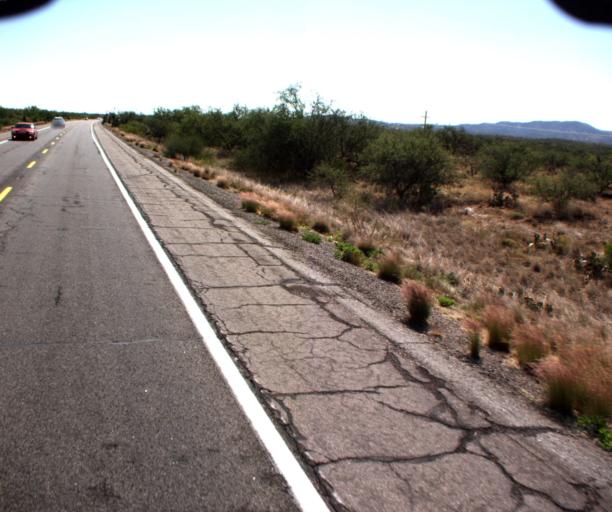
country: US
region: Arizona
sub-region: Pinal County
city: Oracle
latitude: 32.6084
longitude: -110.8522
